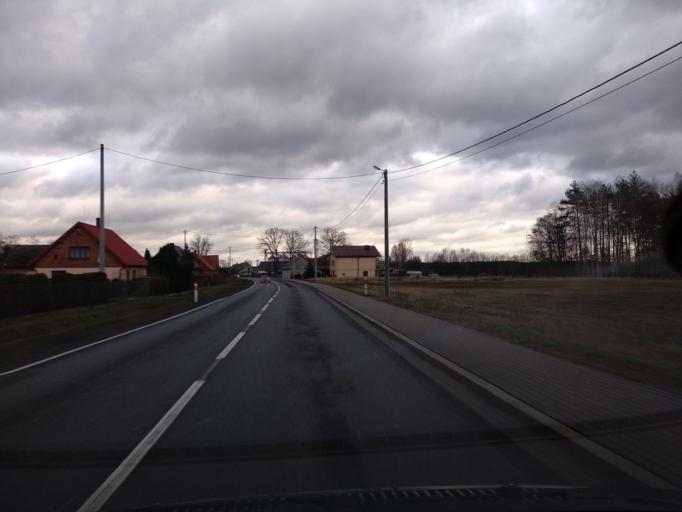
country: PL
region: Lower Silesian Voivodeship
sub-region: Powiat olesnicki
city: Miedzyborz
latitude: 51.4356
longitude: 17.6943
